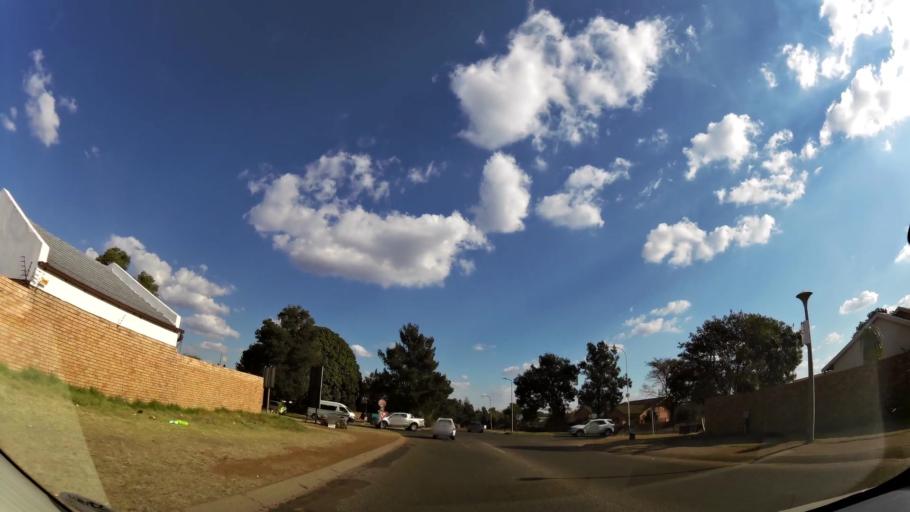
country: ZA
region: Mpumalanga
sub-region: Nkangala District Municipality
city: Witbank
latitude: -25.9034
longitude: 29.2442
